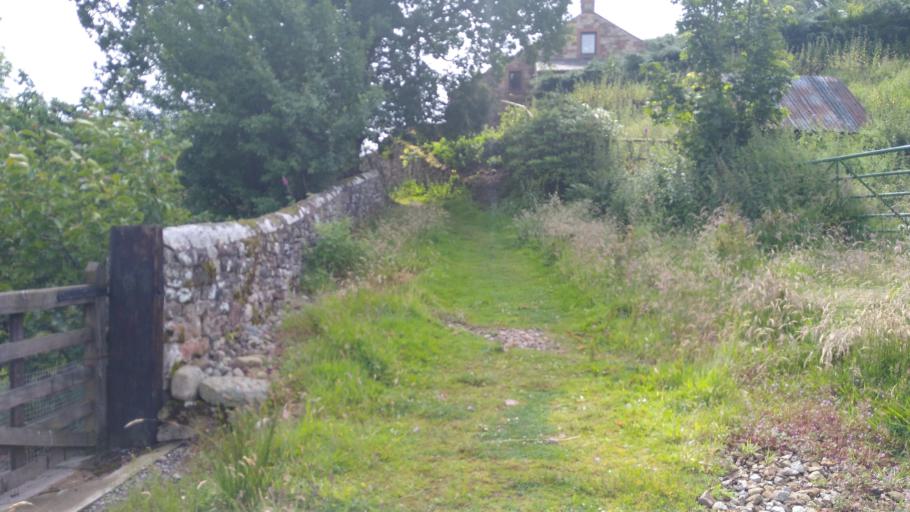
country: GB
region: England
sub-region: Cumbria
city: Brampton
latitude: 54.8998
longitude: -2.7231
